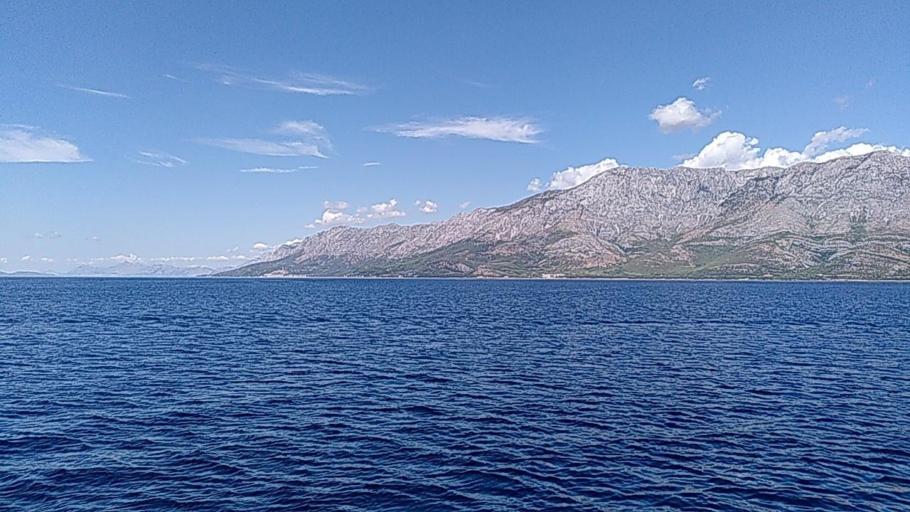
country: HR
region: Dubrovacko-Neretvanska
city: Orebic
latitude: 43.1271
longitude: 17.2039
